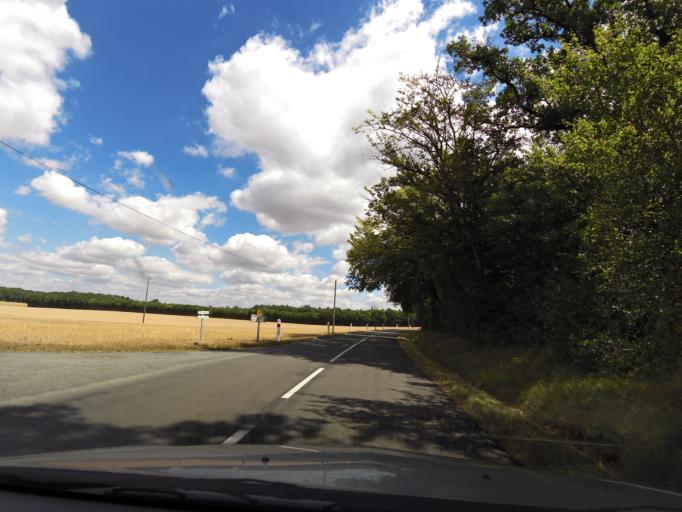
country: FR
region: Poitou-Charentes
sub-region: Departement des Deux-Sevres
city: Beauvoir-sur-Niort
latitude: 46.1556
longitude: -0.4107
